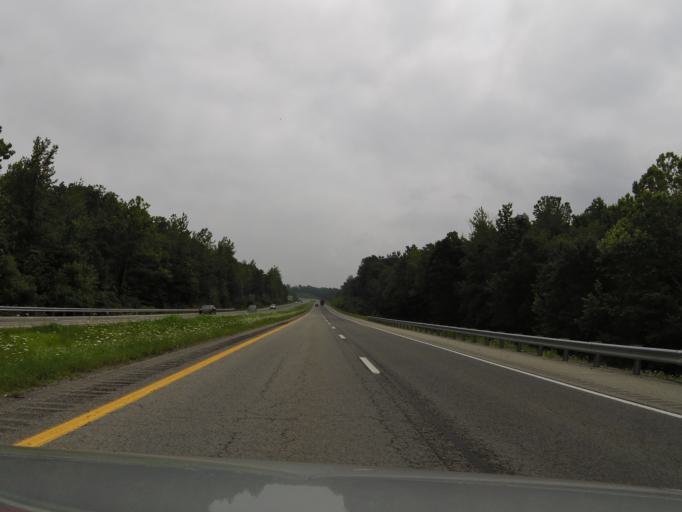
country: US
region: Kentucky
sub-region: Muhlenberg County
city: Central City
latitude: 37.2847
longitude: -87.0944
